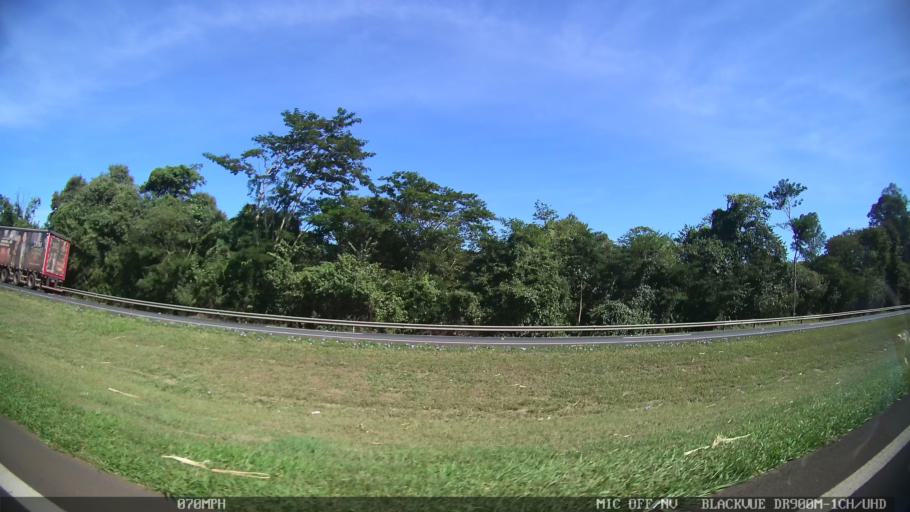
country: BR
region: Sao Paulo
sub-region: Porto Ferreira
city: Porto Ferreira
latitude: -21.8129
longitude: -47.4985
